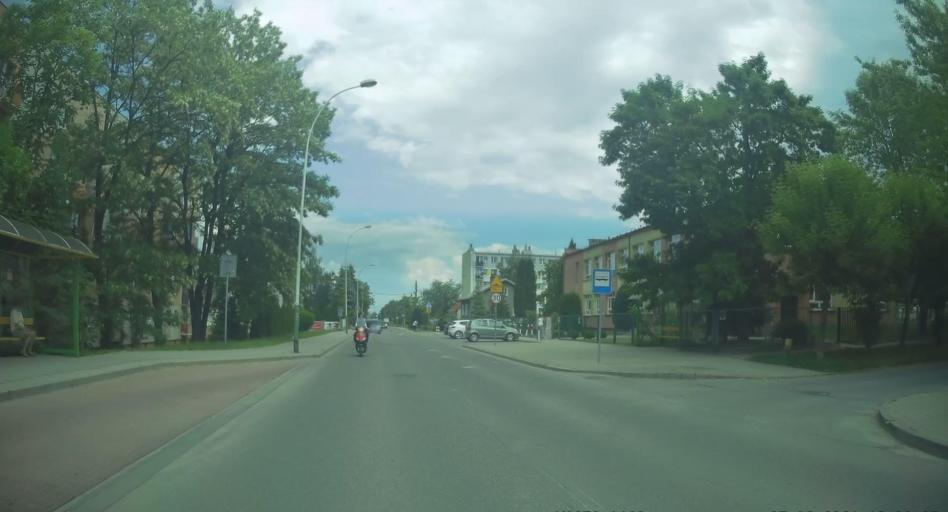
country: PL
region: Subcarpathian Voivodeship
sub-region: Powiat debicki
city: Debica
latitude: 50.0564
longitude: 21.4271
